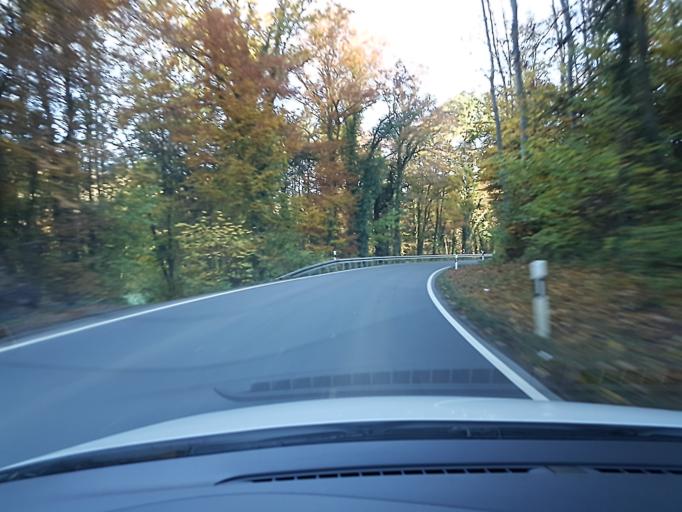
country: DE
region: Baden-Wuerttemberg
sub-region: Regierungsbezirk Stuttgart
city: Neudenau
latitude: 49.2812
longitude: 9.2288
